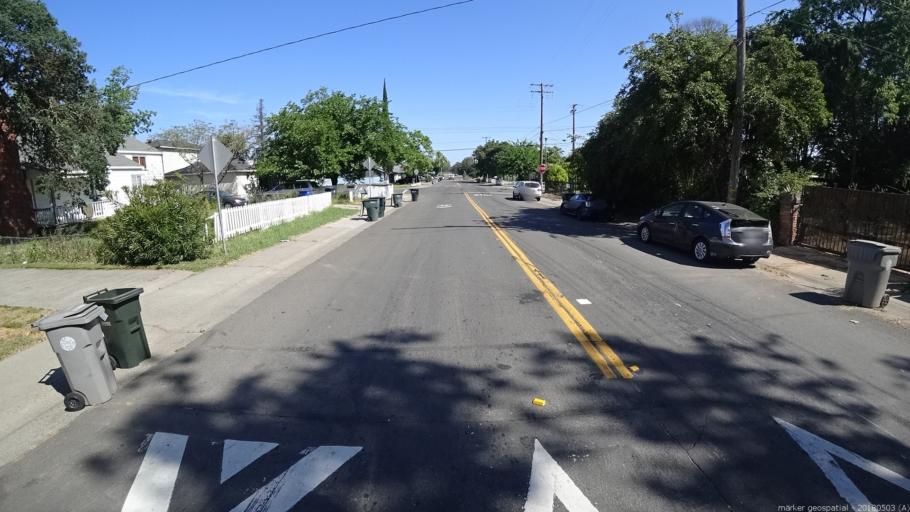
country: US
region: California
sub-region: Sacramento County
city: Arden-Arcade
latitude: 38.6342
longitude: -121.4161
